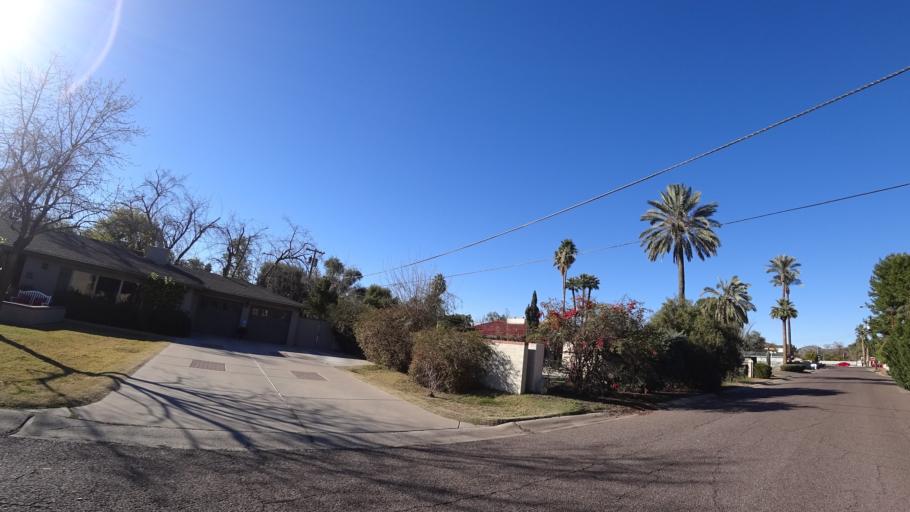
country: US
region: Arizona
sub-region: Maricopa County
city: Phoenix
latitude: 33.5224
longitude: -112.0802
